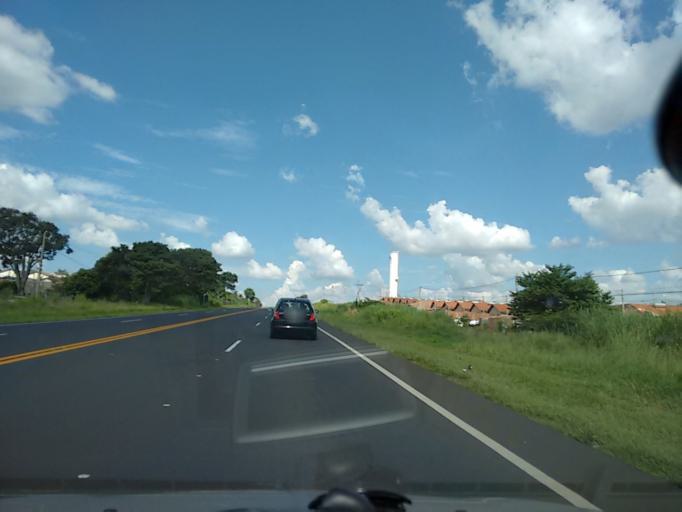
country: BR
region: Sao Paulo
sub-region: Marilia
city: Marilia
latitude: -22.1571
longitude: -50.0163
